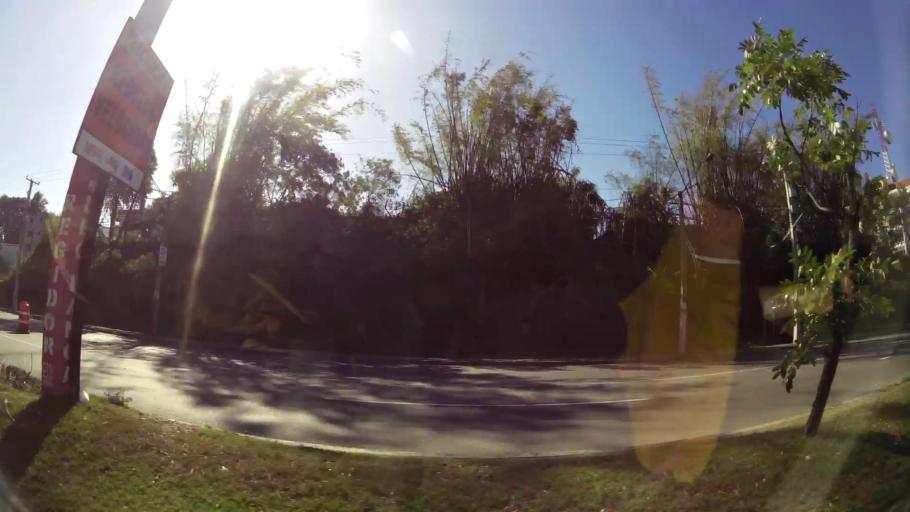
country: DO
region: Nacional
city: Bella Vista
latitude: 18.4532
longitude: -69.9832
